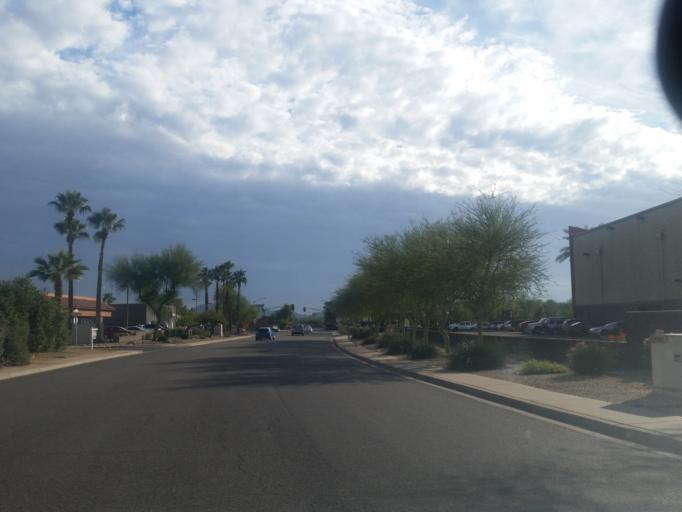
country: US
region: Arizona
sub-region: Maricopa County
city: Paradise Valley
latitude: 33.6424
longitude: -112.0076
